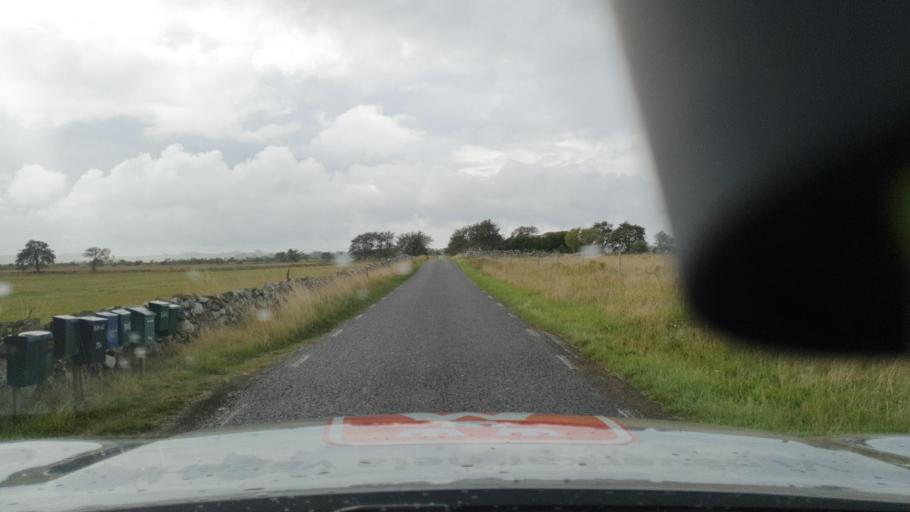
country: SE
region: Gotland
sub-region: Gotland
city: Hemse
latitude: 57.0012
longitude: 18.3635
